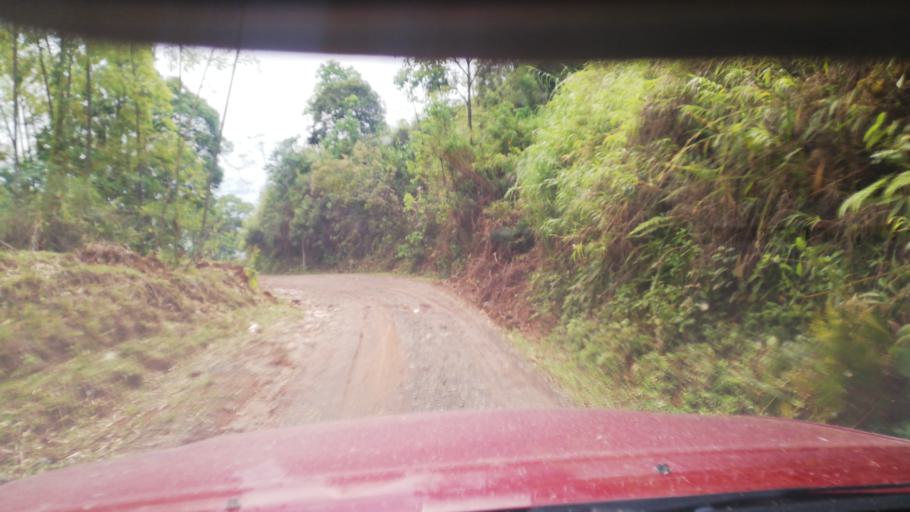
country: CO
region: Risaralda
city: La Virginia
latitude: 4.8777
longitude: -75.9436
